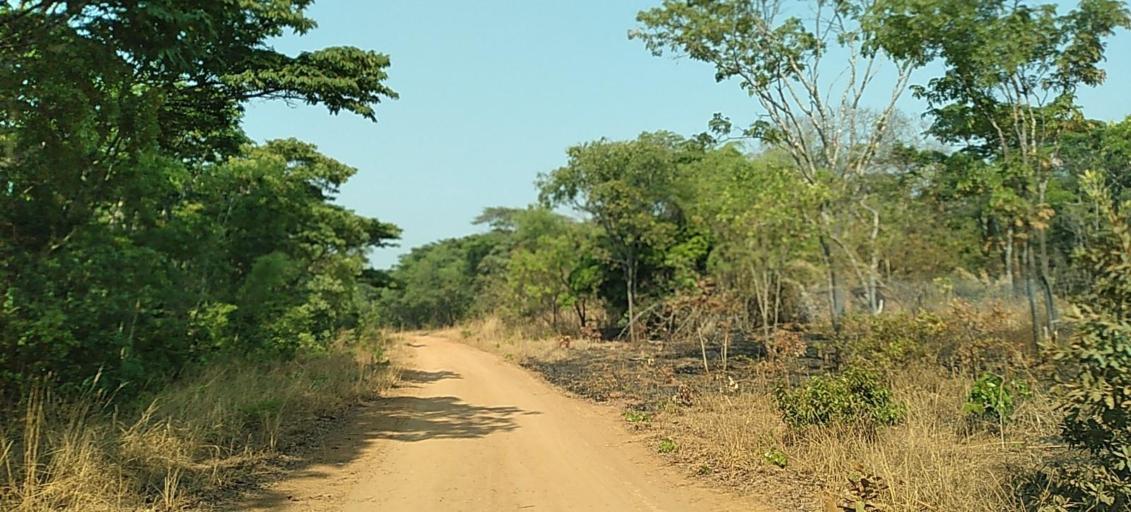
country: ZM
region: Copperbelt
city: Chingola
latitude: -12.8815
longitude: 27.4299
